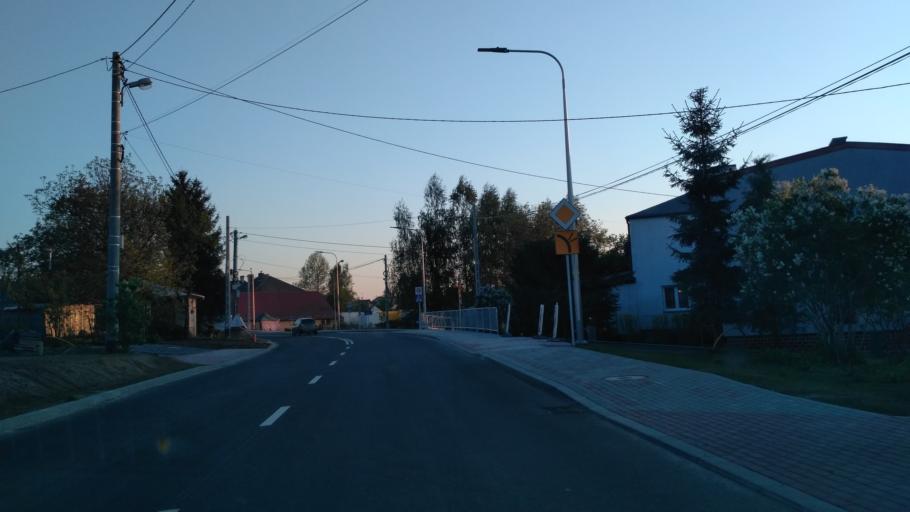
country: PL
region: Subcarpathian Voivodeship
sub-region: Powiat rzeszowski
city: Tyczyn
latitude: 50.0083
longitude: 22.0344
